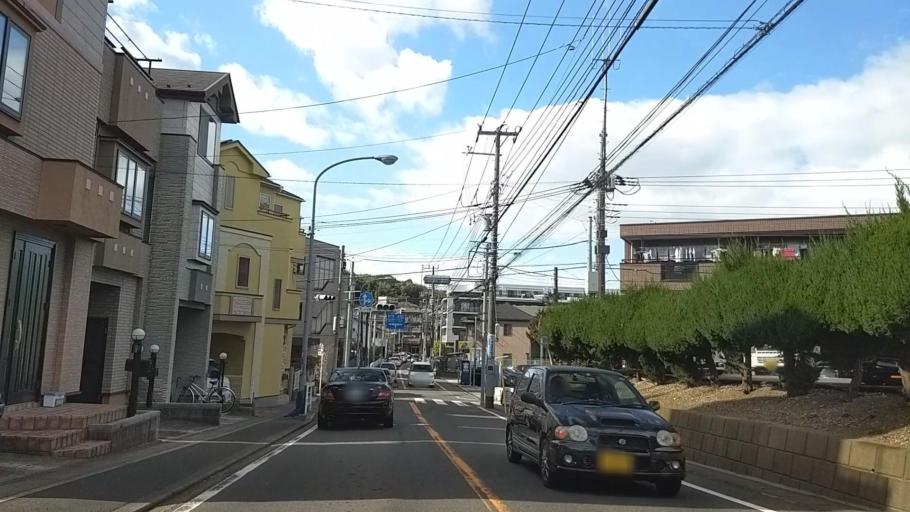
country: JP
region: Kanagawa
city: Yokohama
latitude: 35.4916
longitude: 139.6092
